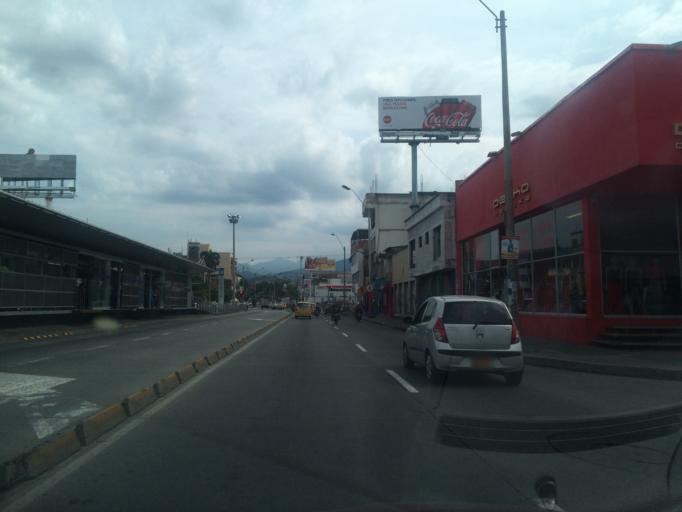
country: CO
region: Valle del Cauca
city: Cali
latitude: 3.4350
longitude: -76.5410
